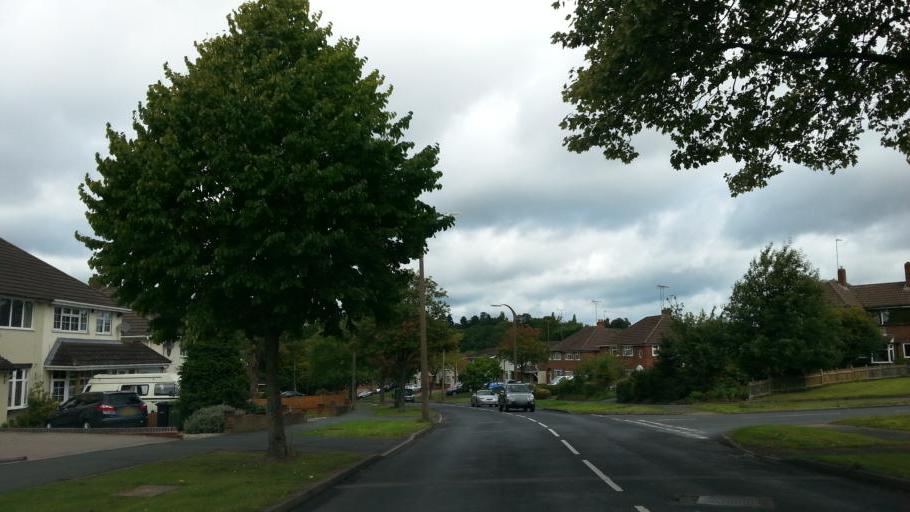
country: GB
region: England
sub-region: Sandwell
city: Cradley Heath
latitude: 52.4513
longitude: -2.0732
